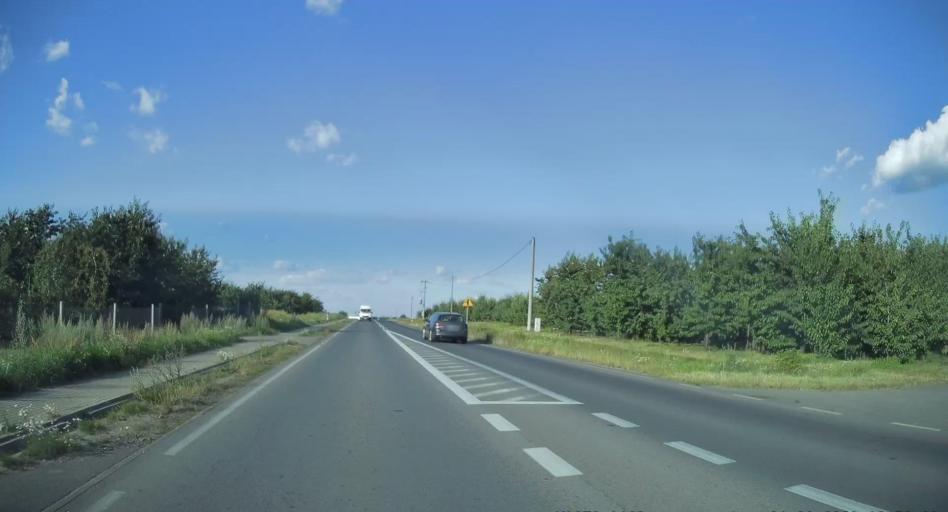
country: PL
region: Masovian Voivodeship
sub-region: Powiat grojecki
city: Belsk Duzy
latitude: 51.8385
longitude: 20.8256
